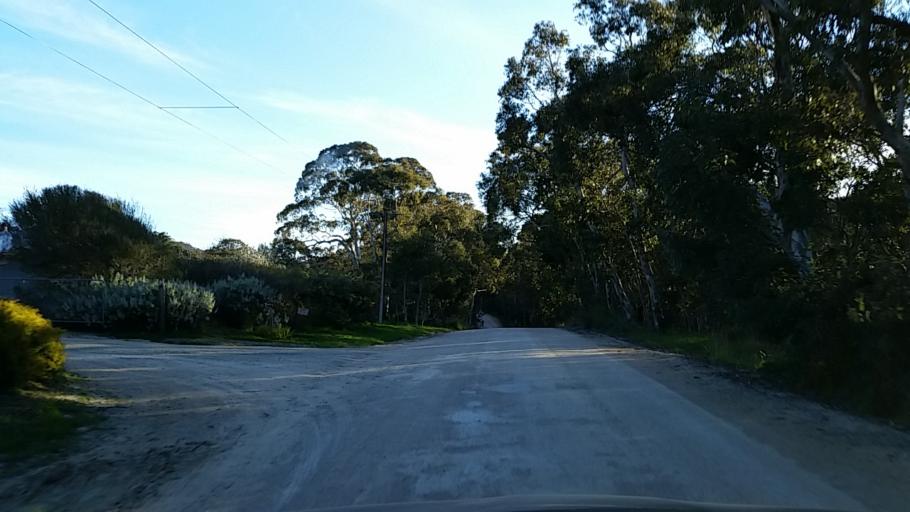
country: AU
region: South Australia
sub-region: Alexandrina
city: Mount Compass
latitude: -35.2966
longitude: 138.6845
